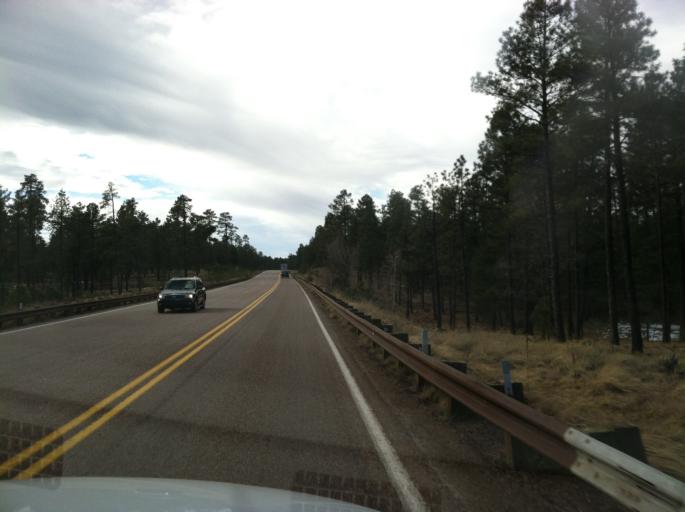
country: US
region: Arizona
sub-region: Navajo County
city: Heber-Overgaard
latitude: 34.3156
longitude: -110.8492
